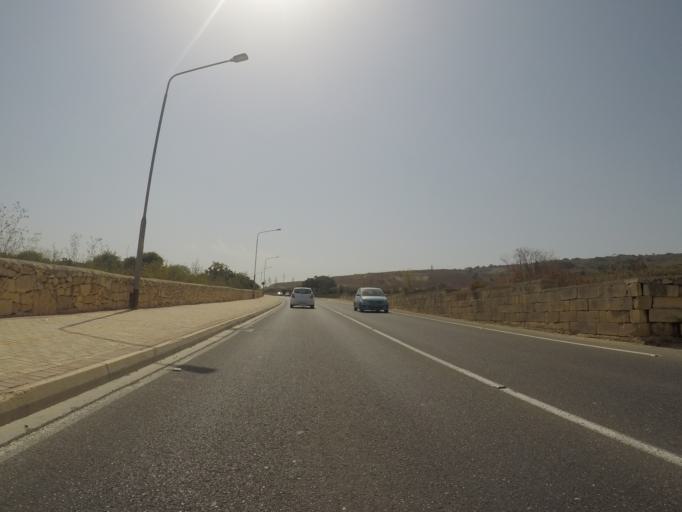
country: MT
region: L-Imgarr
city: Imgarr
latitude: 35.9147
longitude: 14.3888
